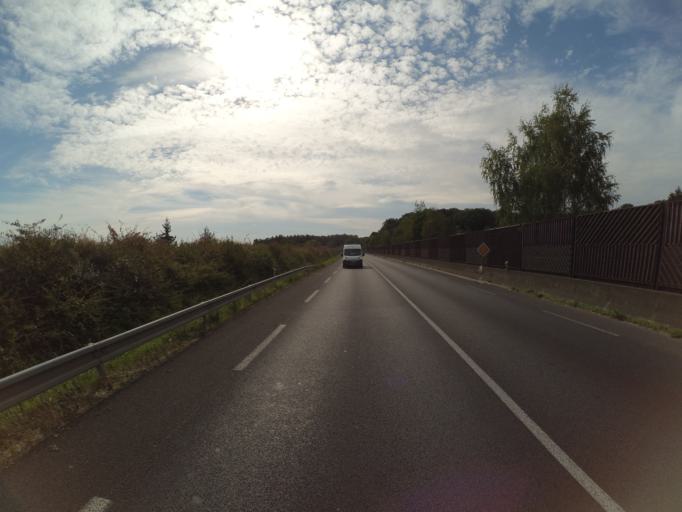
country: FR
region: Pays de la Loire
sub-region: Departement de Maine-et-Loire
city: Saumur
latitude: 47.2594
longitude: -0.0974
